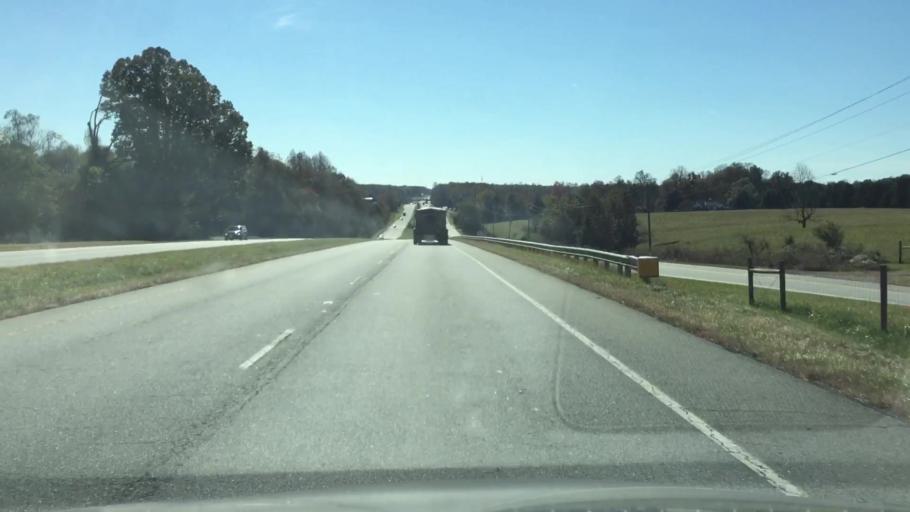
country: US
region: North Carolina
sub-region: Guilford County
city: McLeansville
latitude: 36.1865
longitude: -79.7053
